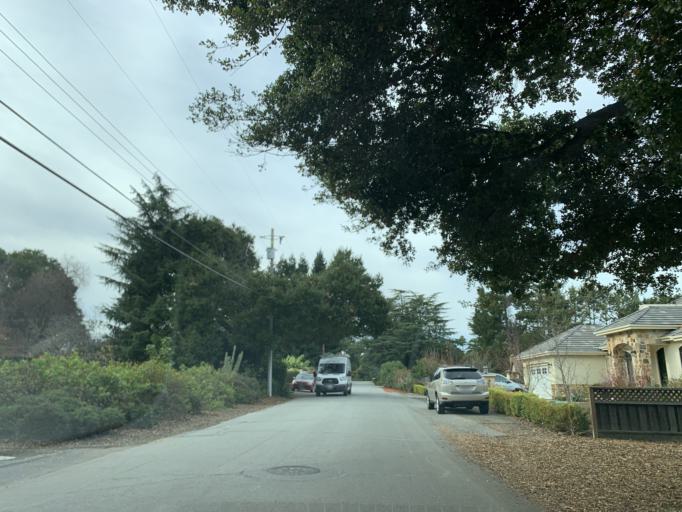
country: US
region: California
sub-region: Santa Clara County
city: Los Altos
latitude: 37.3755
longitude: -122.1035
